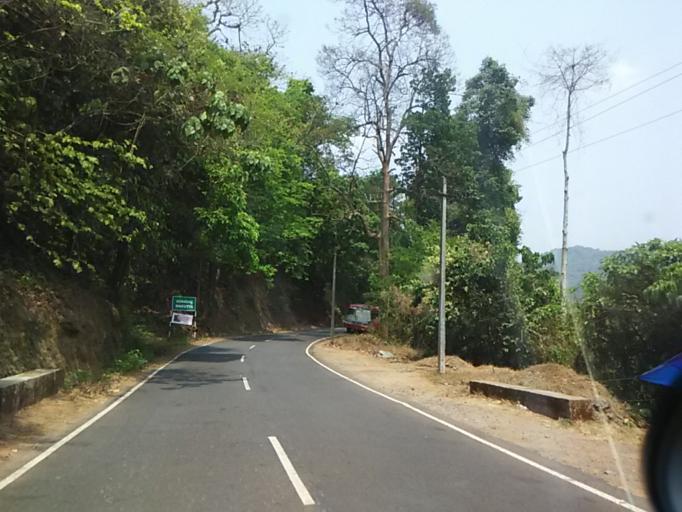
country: IN
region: Karnataka
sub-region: Kodagu
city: Virarajendrapet
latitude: 12.0718
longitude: 75.7207
